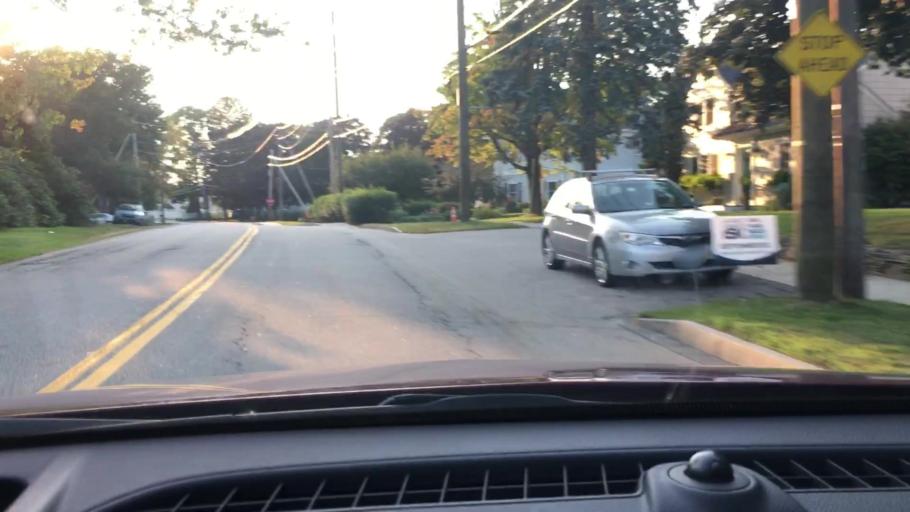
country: US
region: New Hampshire
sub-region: Rockingham County
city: Portsmouth
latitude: 43.0624
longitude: -70.7697
